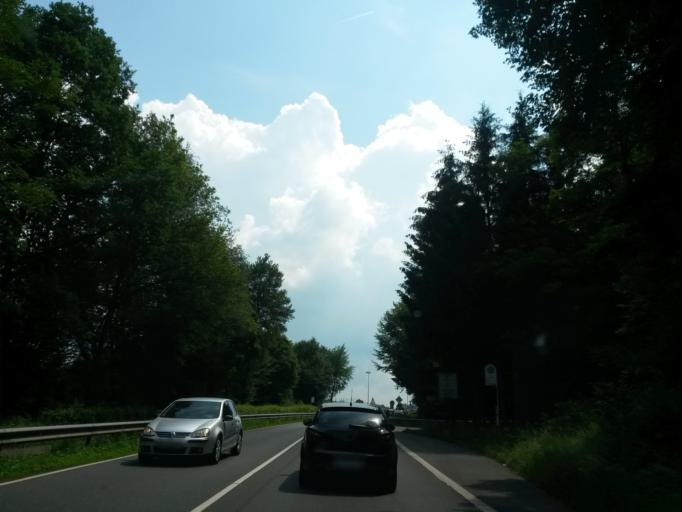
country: DE
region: North Rhine-Westphalia
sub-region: Regierungsbezirk Arnsberg
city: Olpe
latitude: 51.0792
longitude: 7.8504
